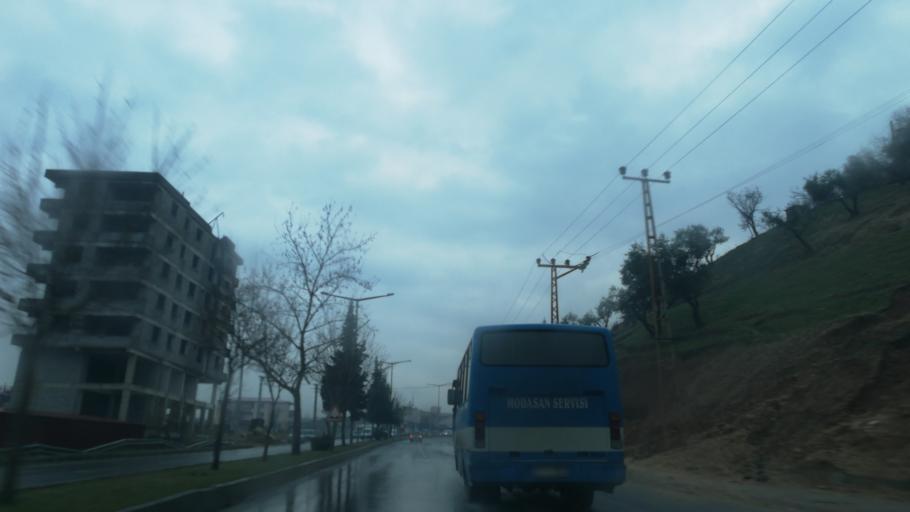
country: TR
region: Kahramanmaras
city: Kahramanmaras
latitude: 37.5818
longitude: 36.9586
